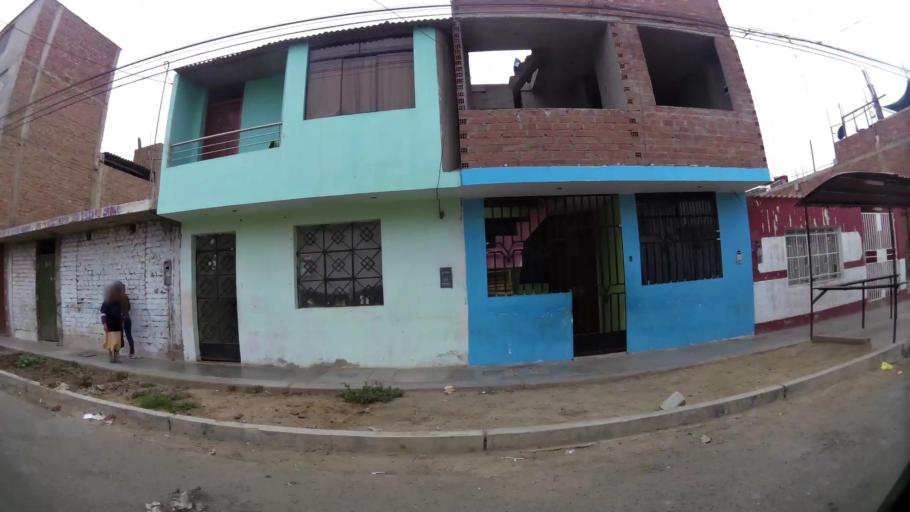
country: PE
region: La Libertad
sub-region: Provincia de Trujillo
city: La Esperanza
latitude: -8.0739
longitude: -79.0542
